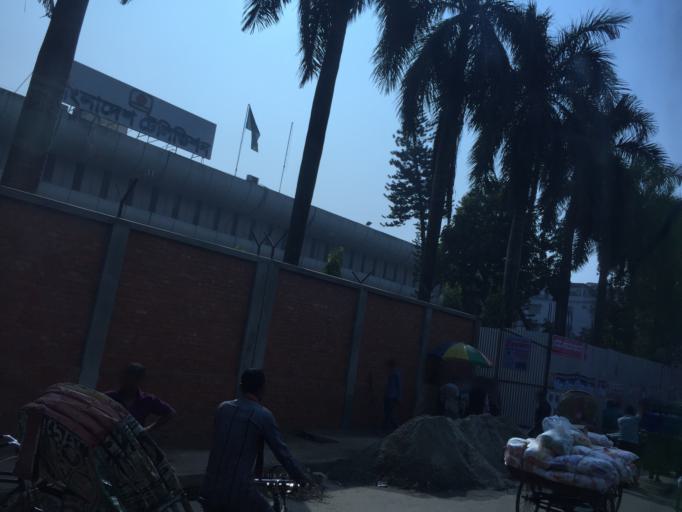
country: BD
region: Dhaka
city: Paltan
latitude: 23.7660
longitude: 90.4221
